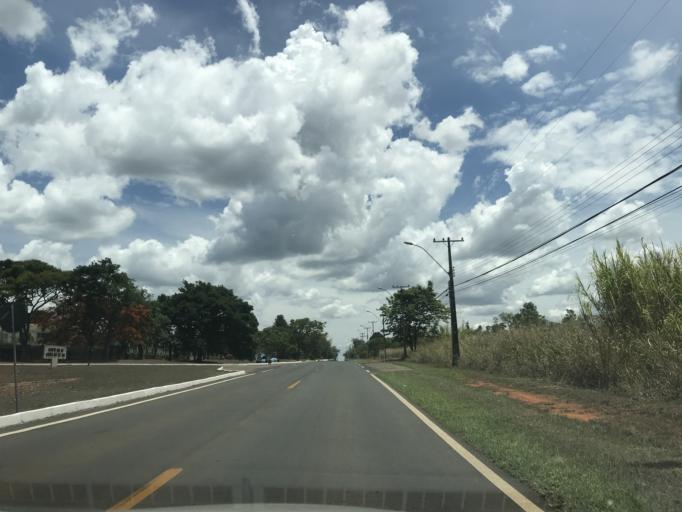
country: BR
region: Federal District
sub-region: Brasilia
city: Brasilia
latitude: -15.9011
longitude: -47.9446
